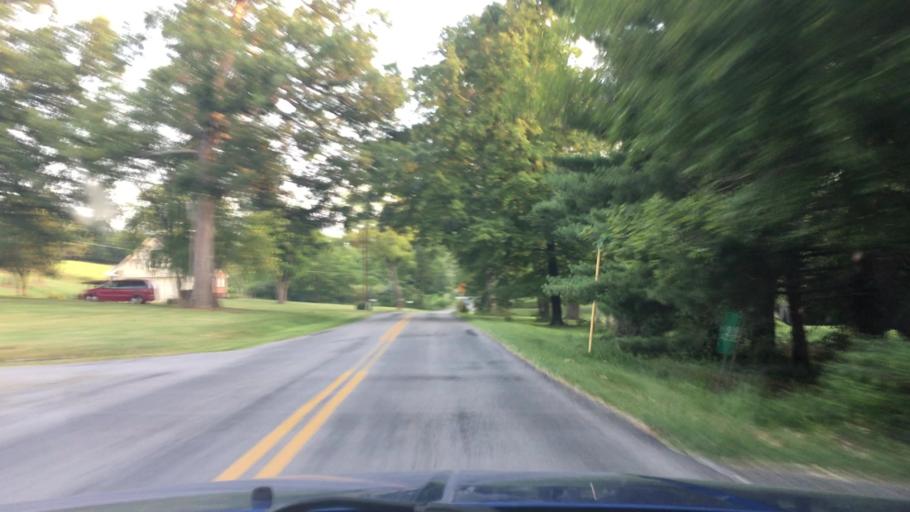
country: US
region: Virginia
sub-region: Augusta County
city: Verona
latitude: 38.2385
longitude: -78.9687
